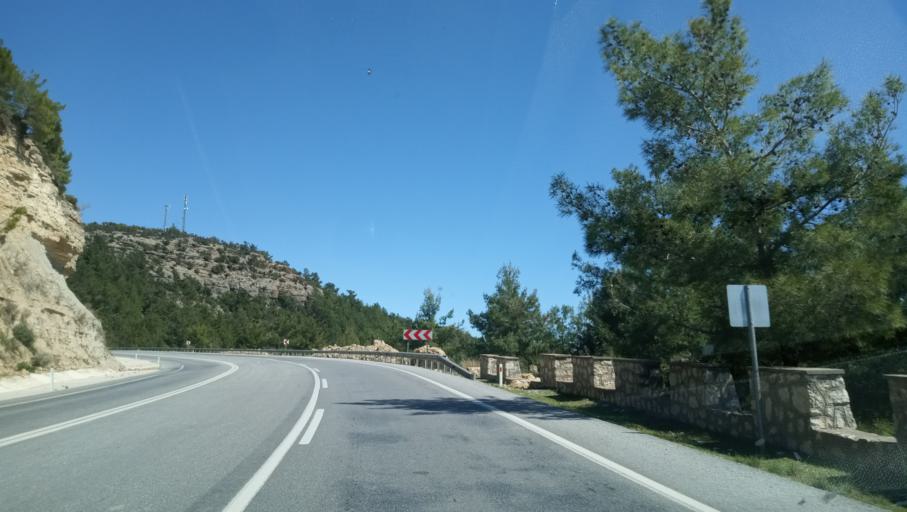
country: TR
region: Antalya
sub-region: Alanya
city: Okurcalar
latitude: 36.7653
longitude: 31.6593
